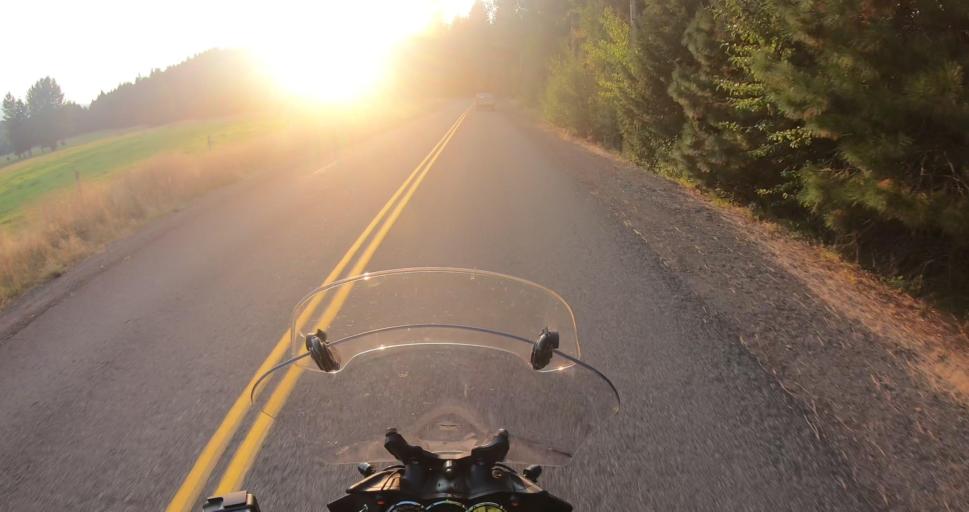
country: US
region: Oregon
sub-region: Hood River County
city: Odell
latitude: 45.4791
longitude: -121.5996
